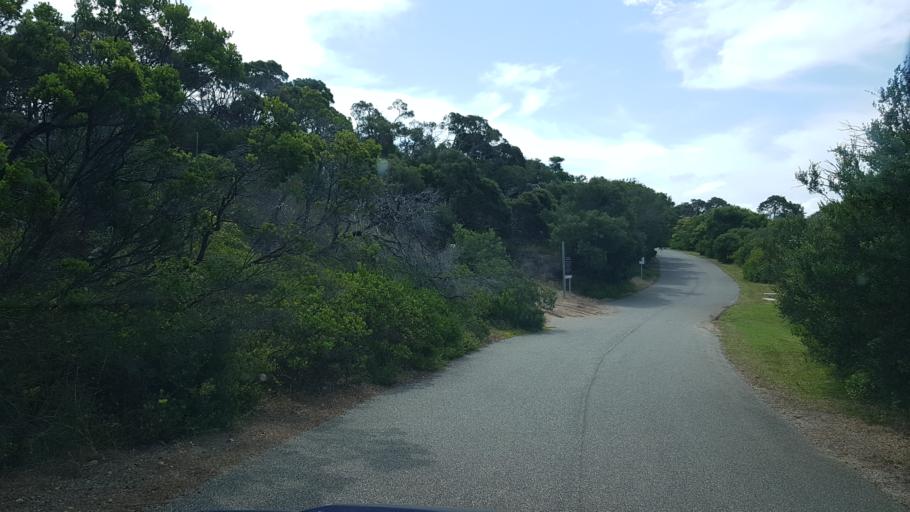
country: AU
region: Victoria
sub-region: Mornington Peninsula
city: Sorrento
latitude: -38.3166
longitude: 144.7023
